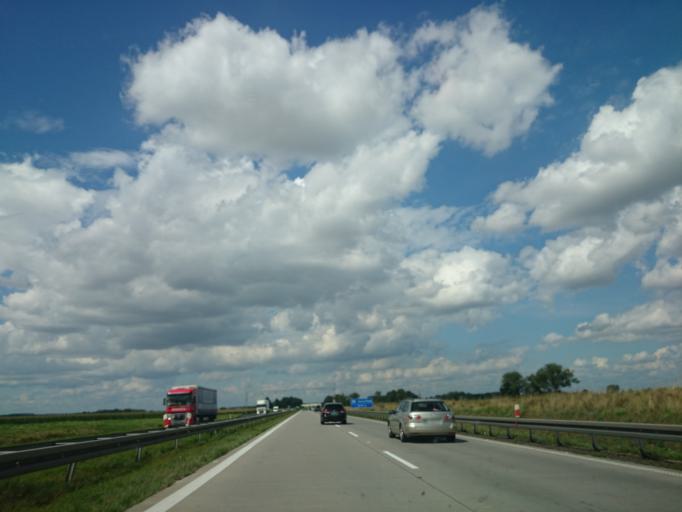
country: PL
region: Lower Silesian Voivodeship
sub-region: Powiat sredzki
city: Ciechow
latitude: 51.0491
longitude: 16.5677
